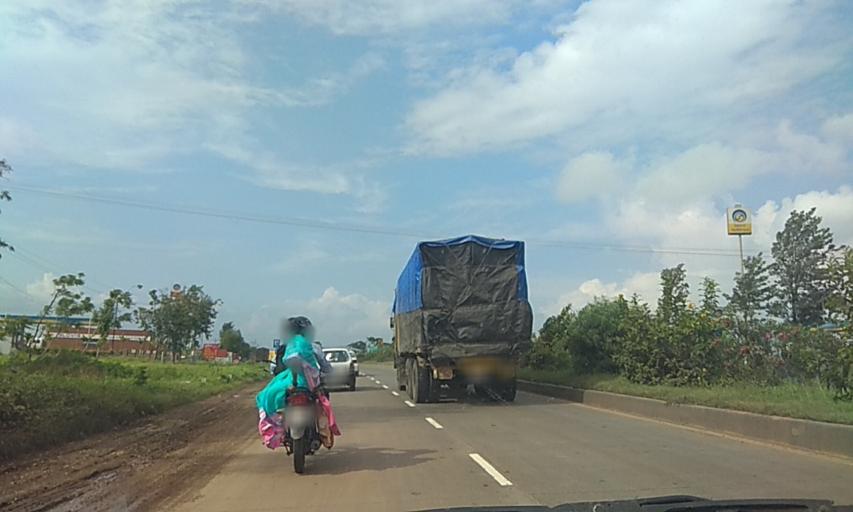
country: IN
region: Maharashtra
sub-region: Kolhapur
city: Kodoli
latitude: 16.8100
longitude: 74.2854
